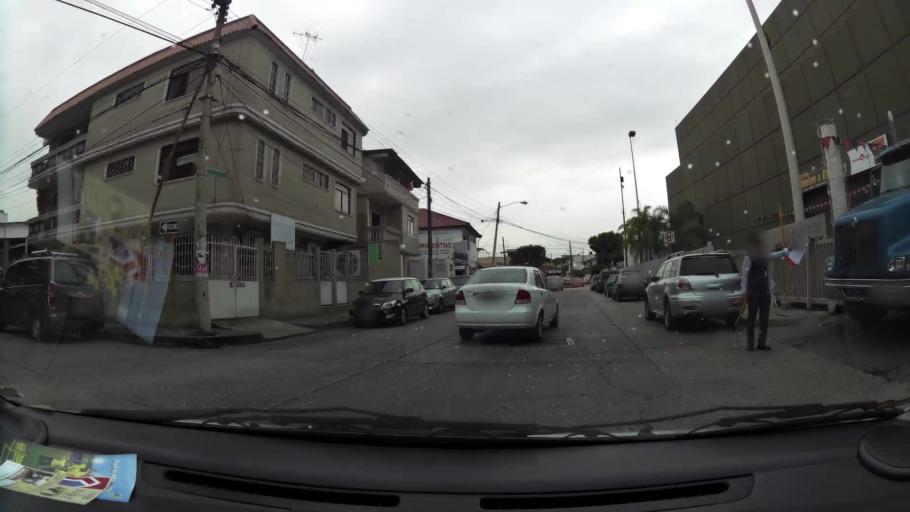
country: EC
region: Guayas
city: Eloy Alfaro
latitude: -2.1544
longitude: -79.8915
